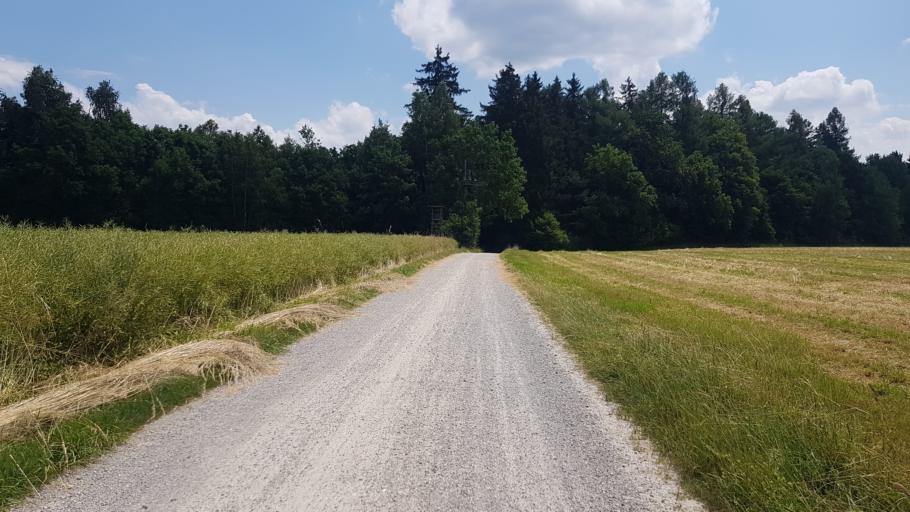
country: DE
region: Bavaria
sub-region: Upper Bavaria
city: Gauting
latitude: 48.0534
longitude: 11.4175
